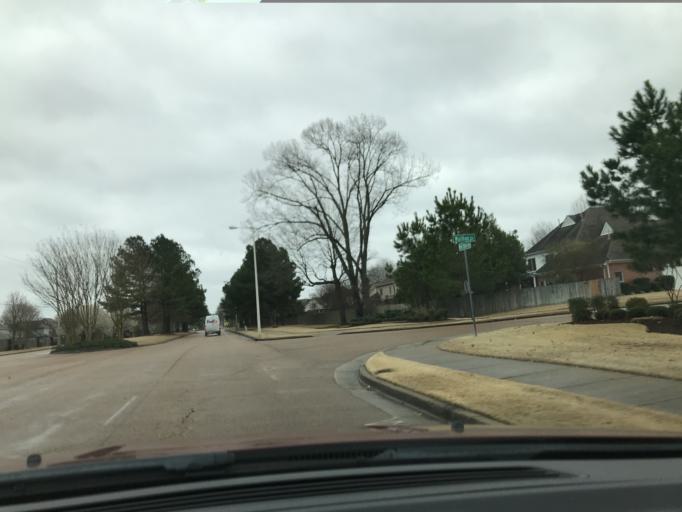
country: US
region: Tennessee
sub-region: Shelby County
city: Collierville
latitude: 35.0854
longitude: -89.6957
